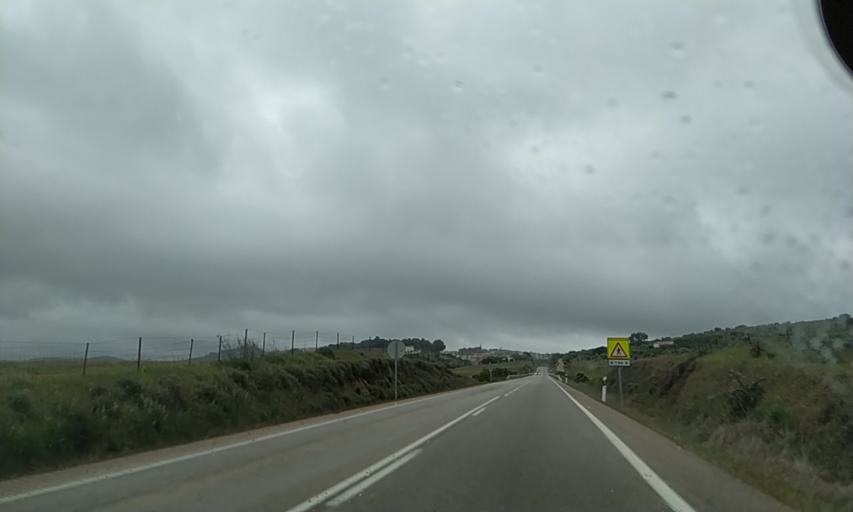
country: ES
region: Extremadura
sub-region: Provincia de Caceres
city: Caceres
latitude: 39.4938
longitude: -6.3854
